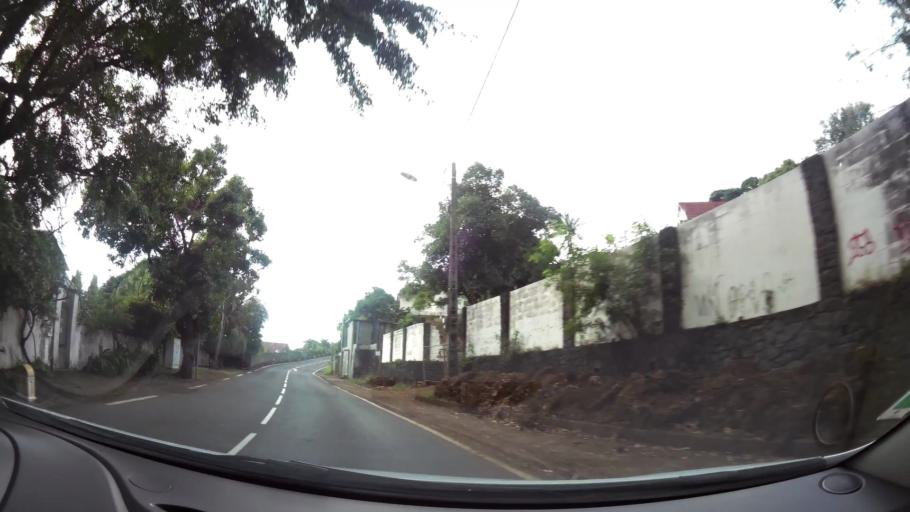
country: RE
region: Reunion
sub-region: Reunion
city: Saint-Denis
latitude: -20.8973
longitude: 55.4422
